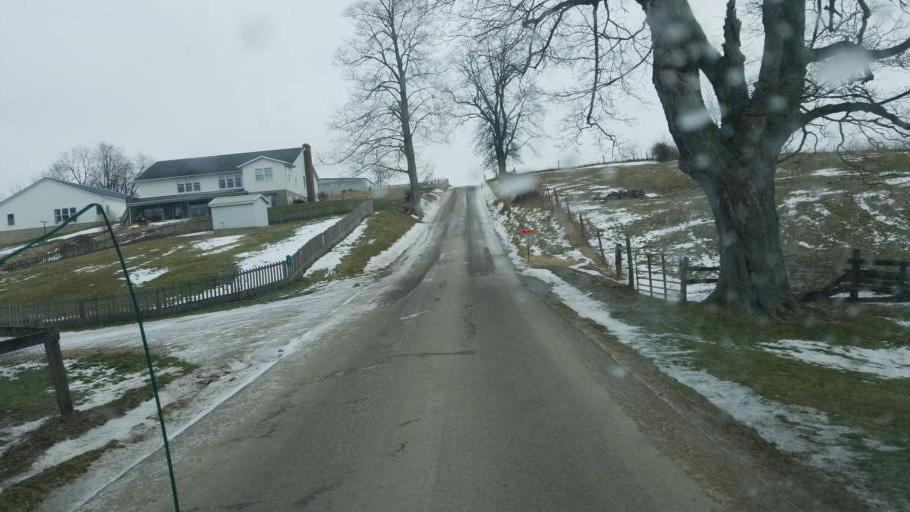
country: US
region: Ohio
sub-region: Wayne County
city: Apple Creek
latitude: 40.6824
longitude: -81.8355
